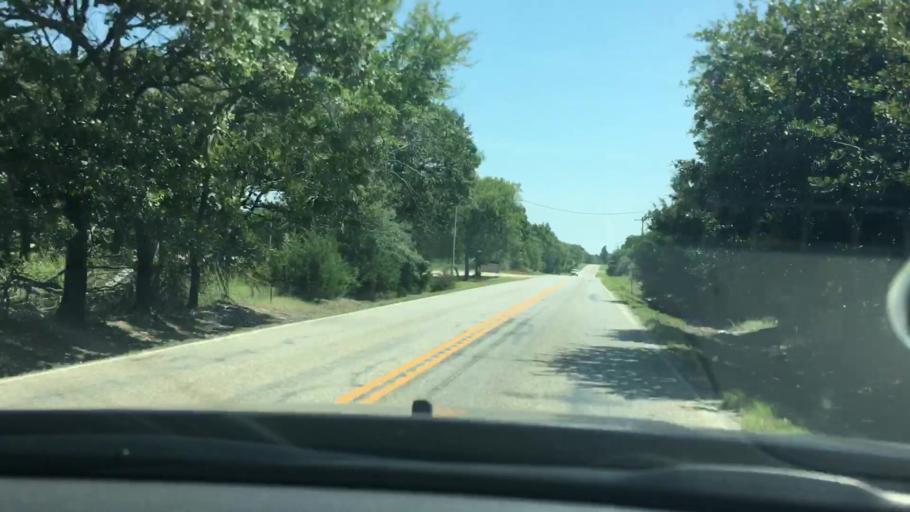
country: US
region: Oklahoma
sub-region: Johnston County
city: Tishomingo
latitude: 34.2377
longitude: -96.5763
